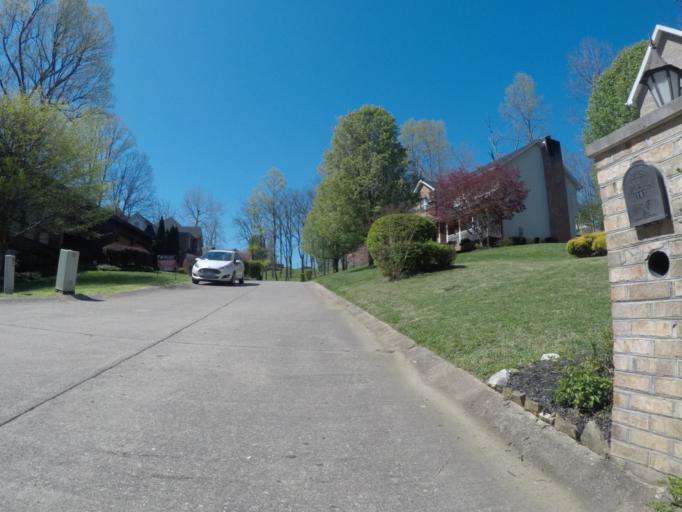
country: US
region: West Virginia
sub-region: Cabell County
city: Pea Ridge
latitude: 38.4154
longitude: -82.3137
